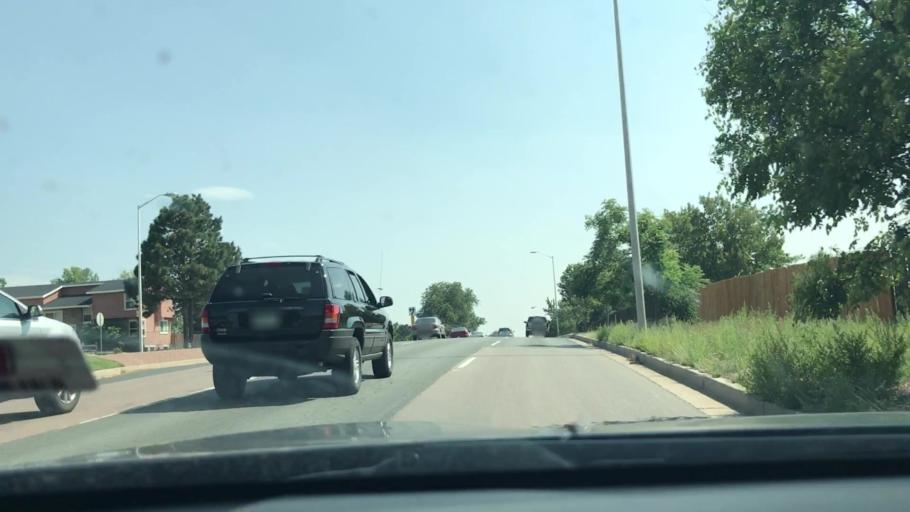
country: US
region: Colorado
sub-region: El Paso County
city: Colorado Springs
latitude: 38.9205
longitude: -104.7754
